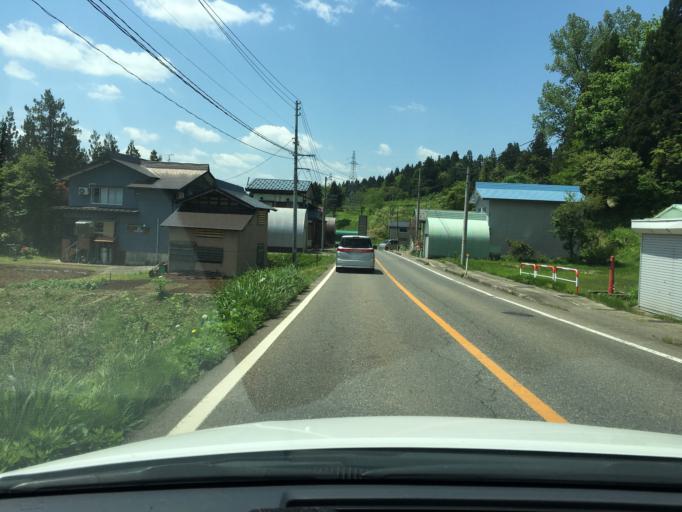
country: JP
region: Niigata
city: Tochio-honcho
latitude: 37.3023
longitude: 138.9974
